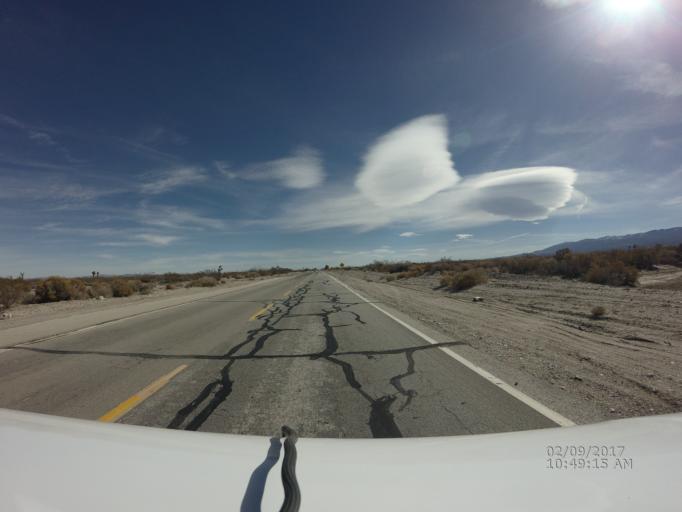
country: US
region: California
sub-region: Los Angeles County
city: Lake Los Angeles
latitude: 34.5425
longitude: -117.8459
